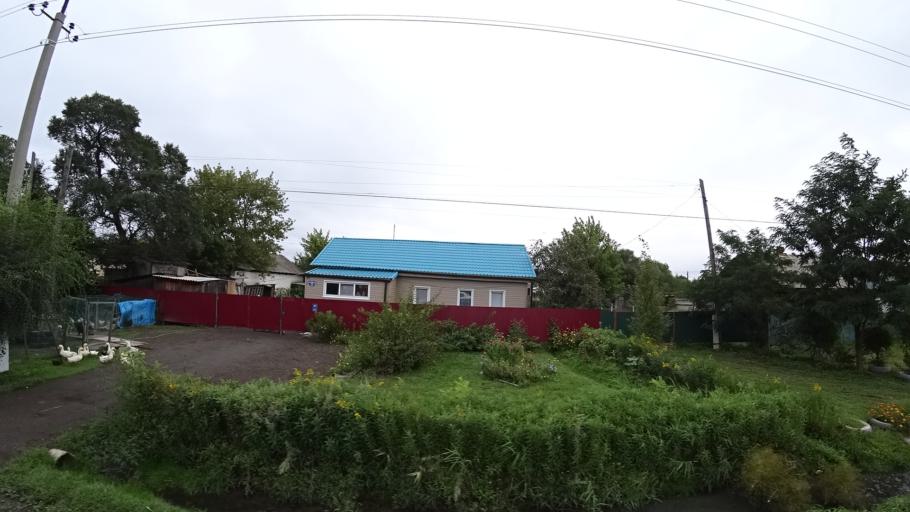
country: RU
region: Primorskiy
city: Chernigovka
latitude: 44.3450
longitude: 132.5817
